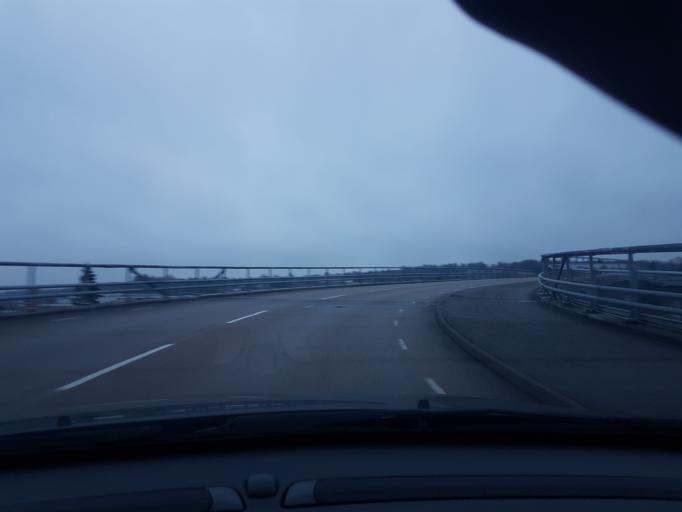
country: SE
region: Vaestra Goetaland
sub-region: Ale Kommun
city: Alvangen
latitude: 57.9608
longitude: 12.1203
